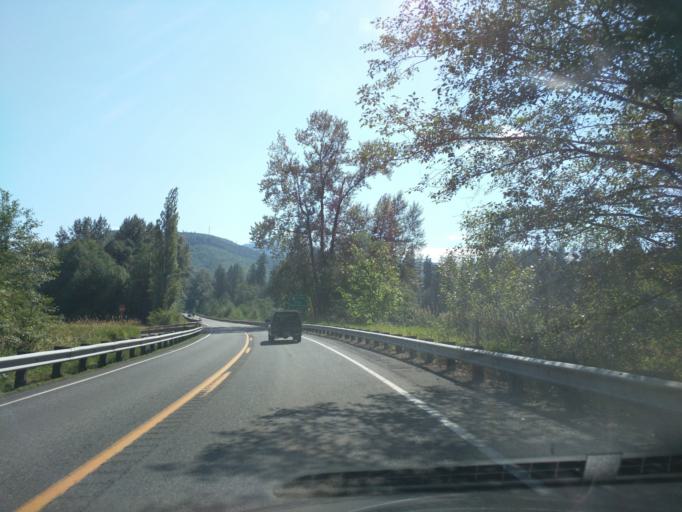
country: US
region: Washington
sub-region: Whatcom County
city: Peaceful Valley
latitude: 48.8211
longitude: -122.1948
